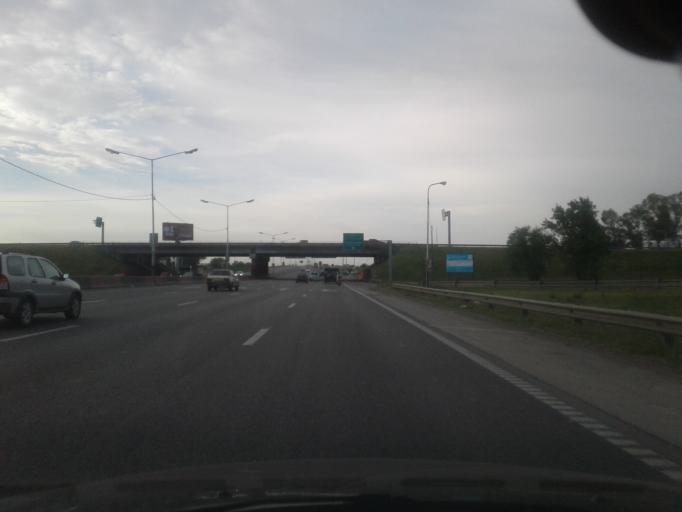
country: AR
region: Santa Fe
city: Perez
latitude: -32.9476
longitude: -60.7223
